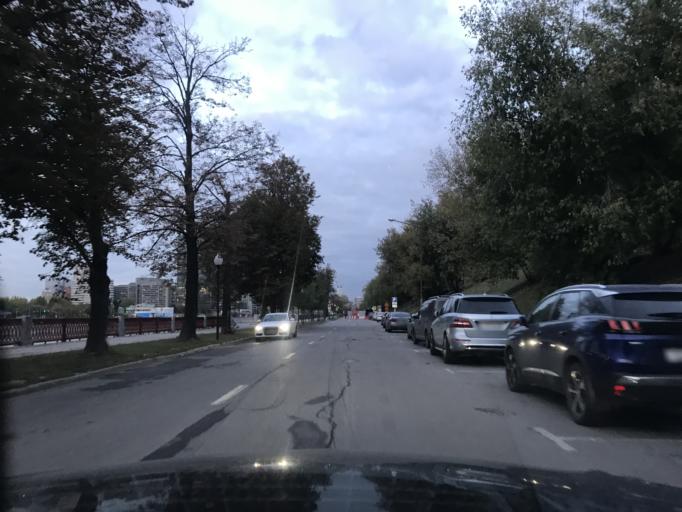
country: RU
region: Moskovskaya
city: Presnenskiy
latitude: 55.7477
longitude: 37.5486
